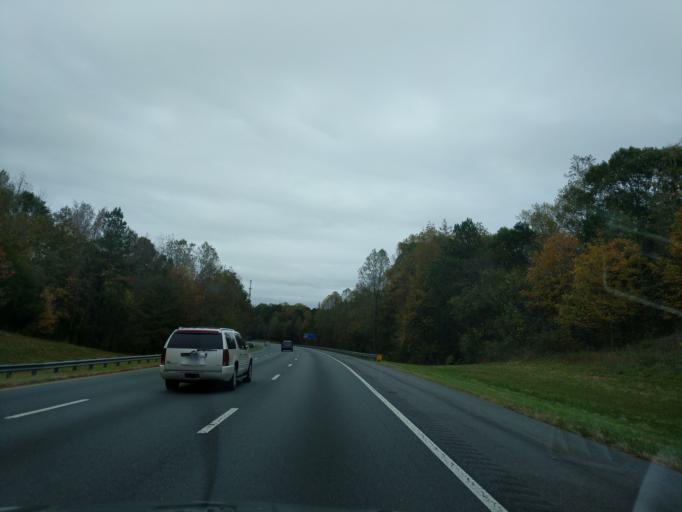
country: US
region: North Carolina
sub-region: Davidson County
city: Lexington
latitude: 35.7882
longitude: -80.2293
